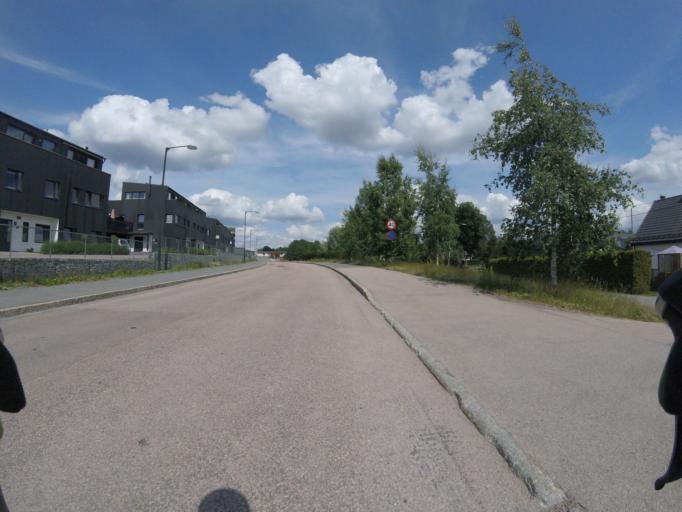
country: NO
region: Akershus
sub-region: Skedsmo
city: Lillestrom
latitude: 59.9752
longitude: 11.0411
